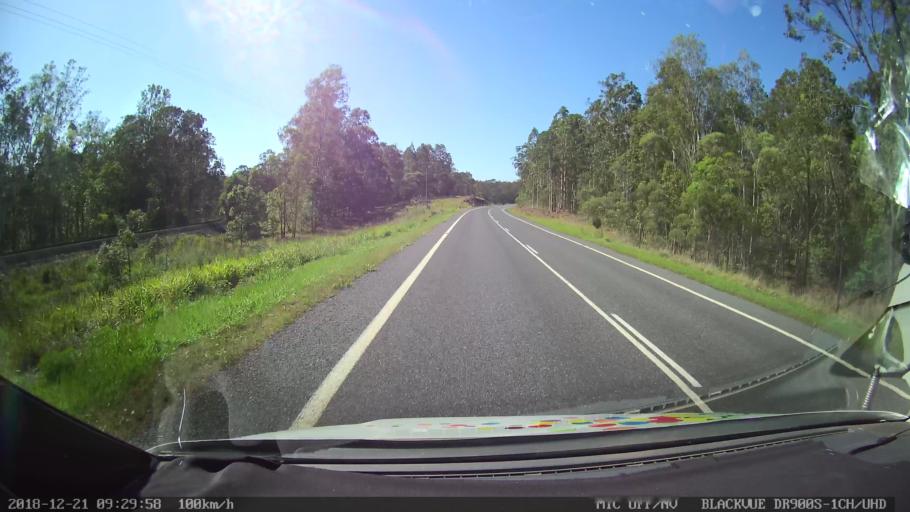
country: AU
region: New South Wales
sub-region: Clarence Valley
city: Maclean
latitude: -29.4396
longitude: 152.9912
